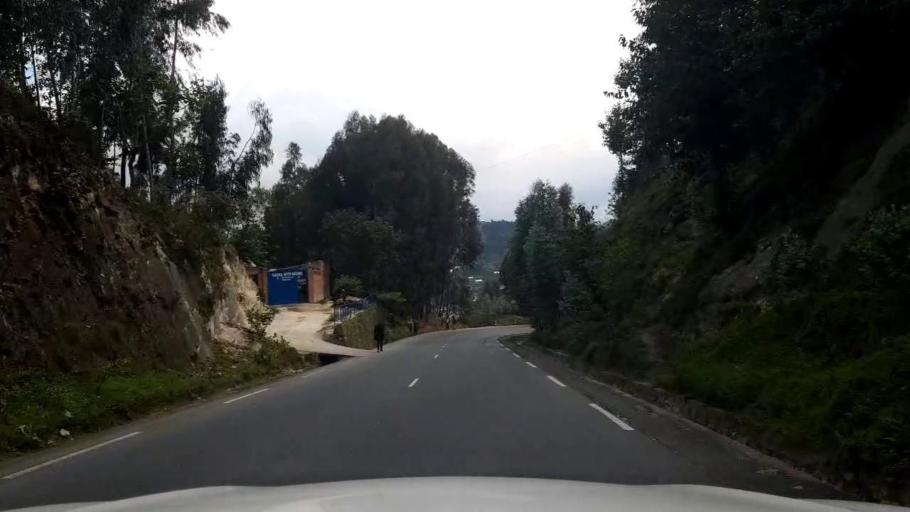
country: RW
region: Northern Province
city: Musanze
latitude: -1.6772
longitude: 29.5176
